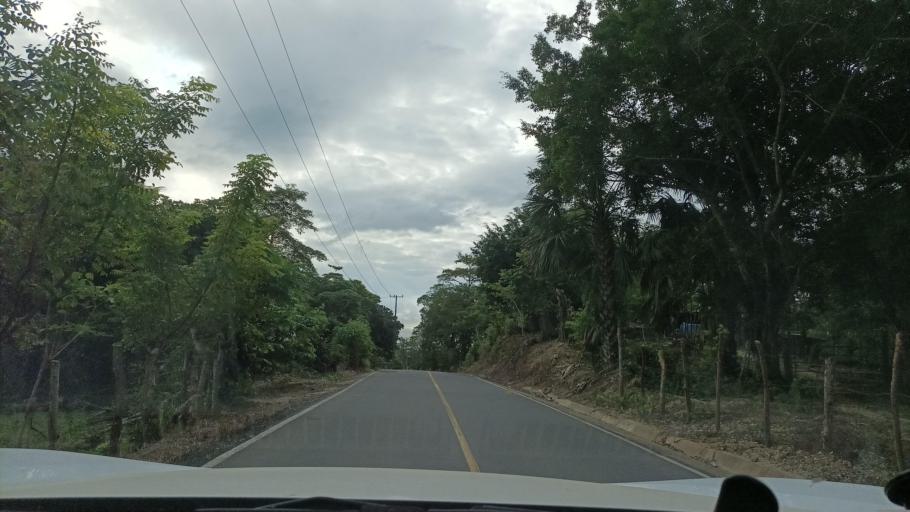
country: MX
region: Veracruz
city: Hidalgotitlan
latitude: 17.7301
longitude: -94.4838
